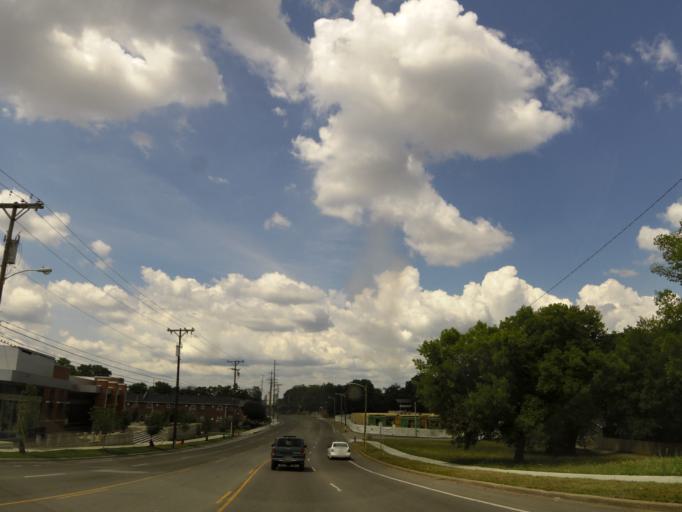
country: US
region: Tennessee
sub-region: Davidson County
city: Nashville
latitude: 36.1368
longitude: -86.7884
